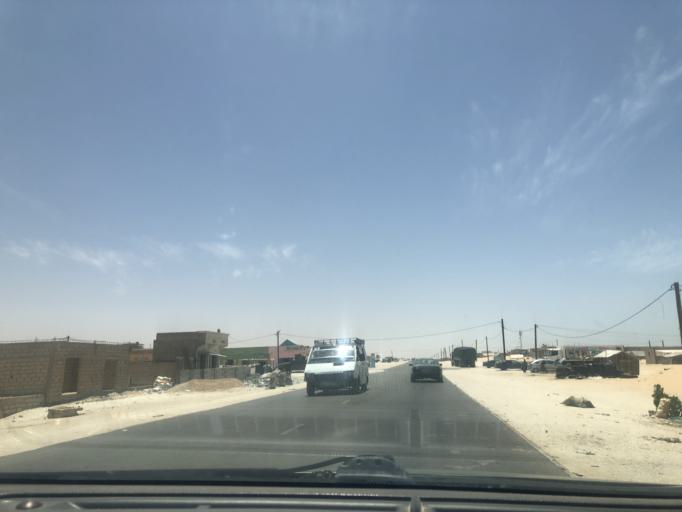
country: MR
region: Nouakchott
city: Nouakchott
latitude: 18.0094
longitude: -15.9595
